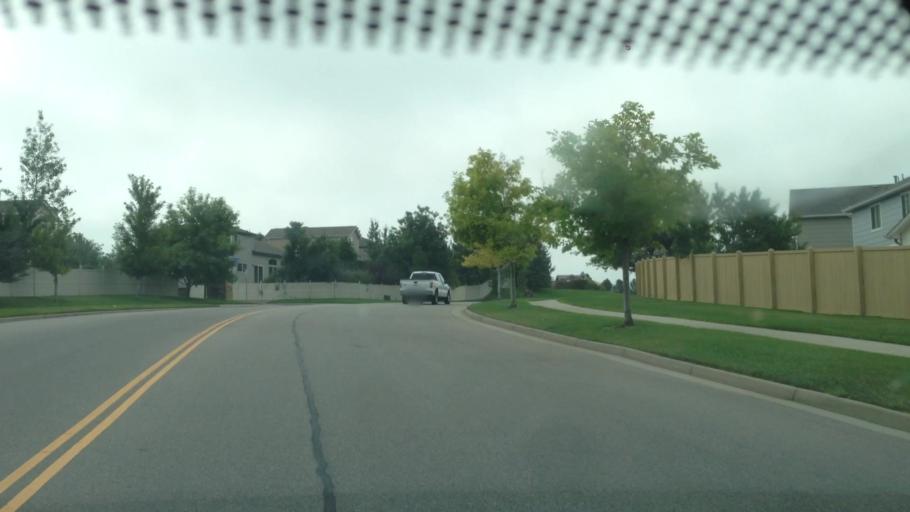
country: US
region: Colorado
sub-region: Douglas County
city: Parker
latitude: 39.6068
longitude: -104.7297
